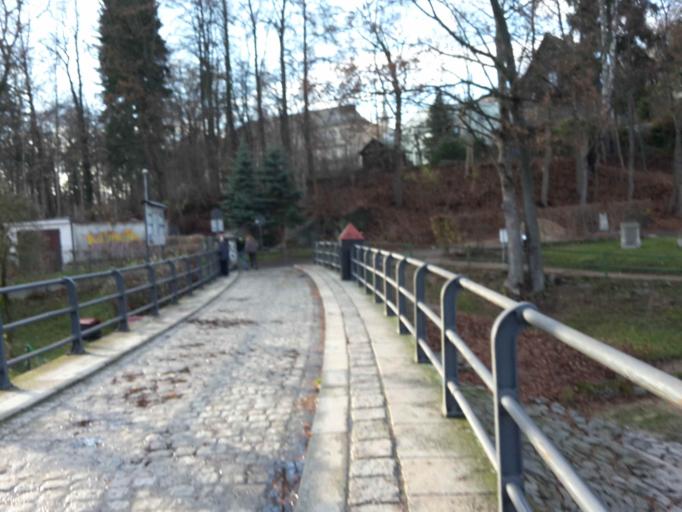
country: CZ
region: Liberecky
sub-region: Okres Liberec
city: Liberec
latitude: 50.7687
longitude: 15.0702
